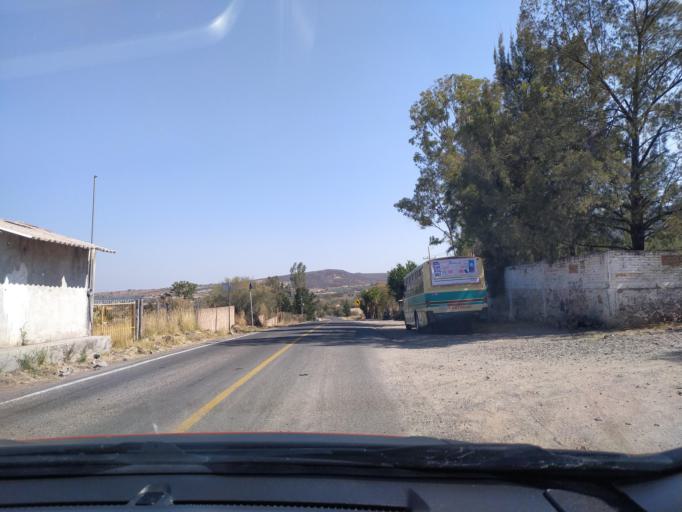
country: MX
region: Guanajuato
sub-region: San Francisco del Rincon
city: San Ignacio de Hidalgo
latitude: 20.8025
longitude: -101.8385
